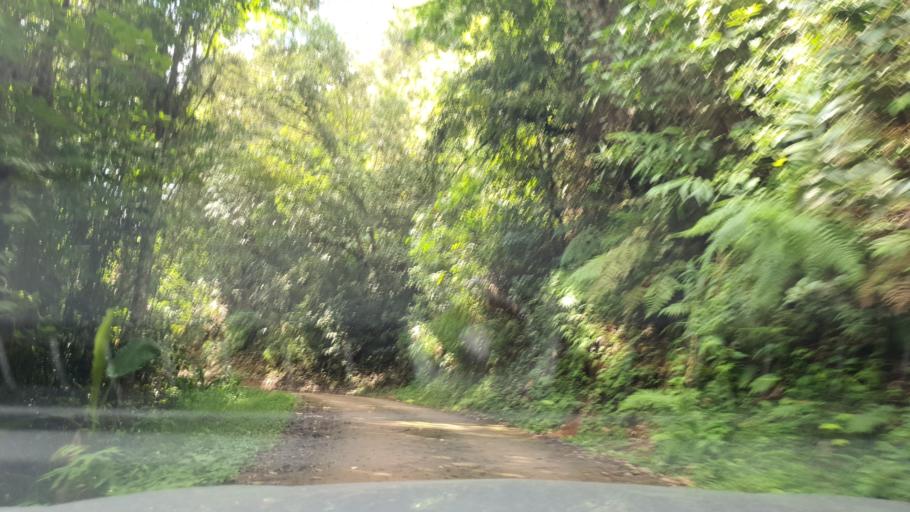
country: TH
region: Chiang Mai
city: Mae On
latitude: 18.9519
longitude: 99.3049
